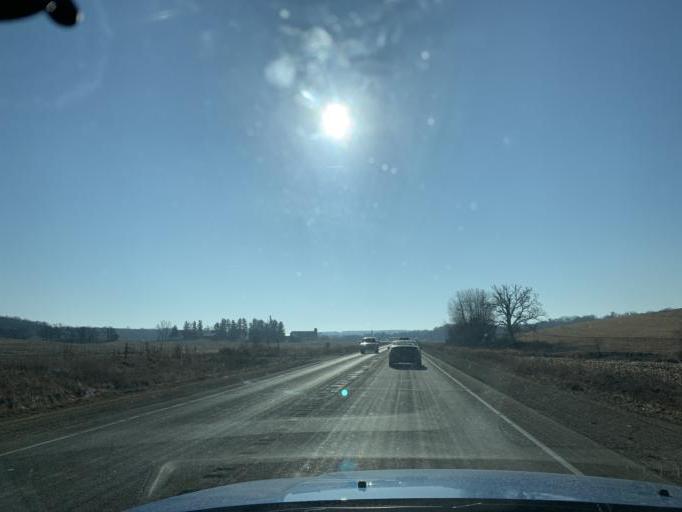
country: US
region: Wisconsin
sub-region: Green County
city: New Glarus
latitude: 42.8311
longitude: -89.6350
